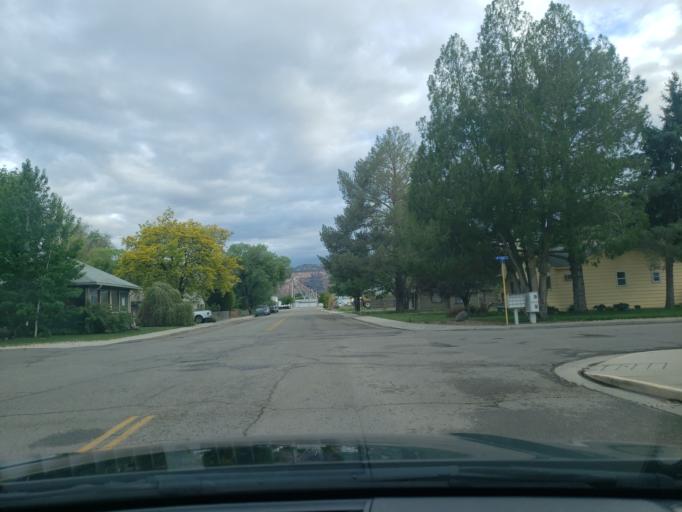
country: US
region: Colorado
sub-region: Mesa County
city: Fruita
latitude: 39.1572
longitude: -108.7314
